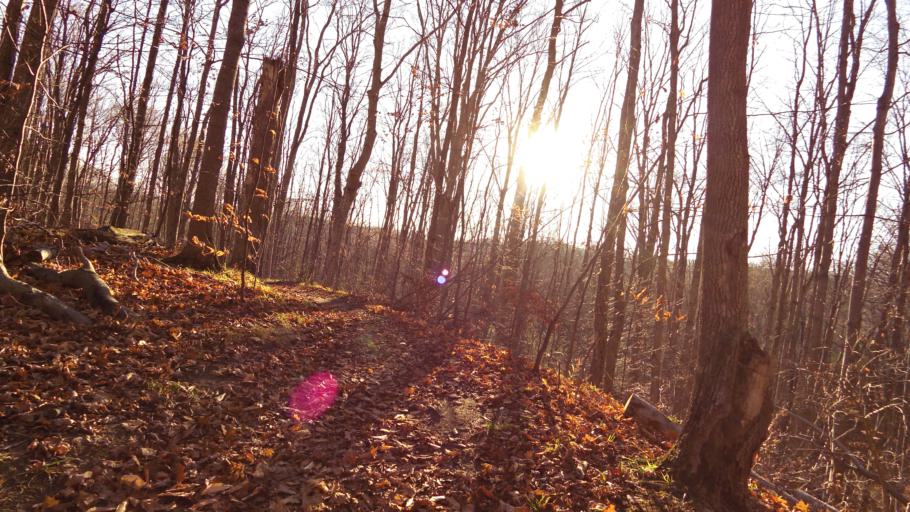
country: CA
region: Ontario
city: Orangeville
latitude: 43.9915
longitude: -80.0578
